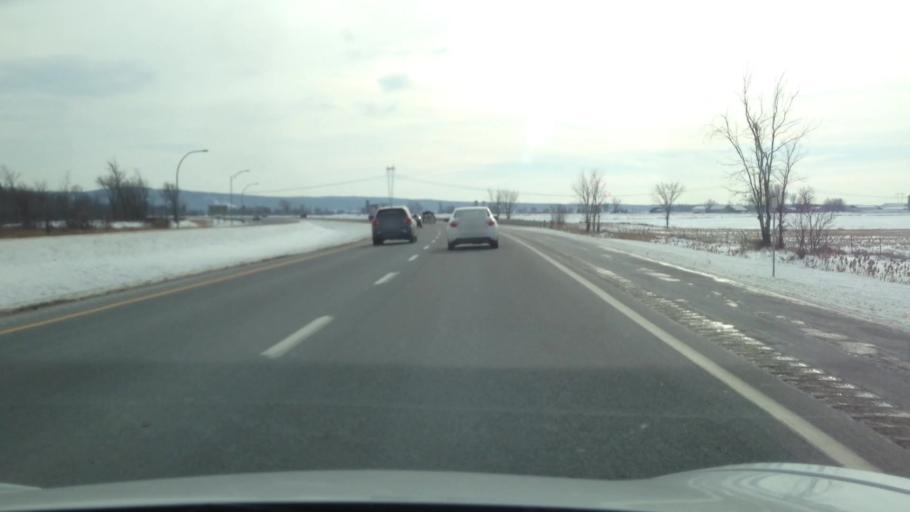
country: CA
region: Quebec
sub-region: Monteregie
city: Rigaud
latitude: 45.5133
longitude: -74.3738
